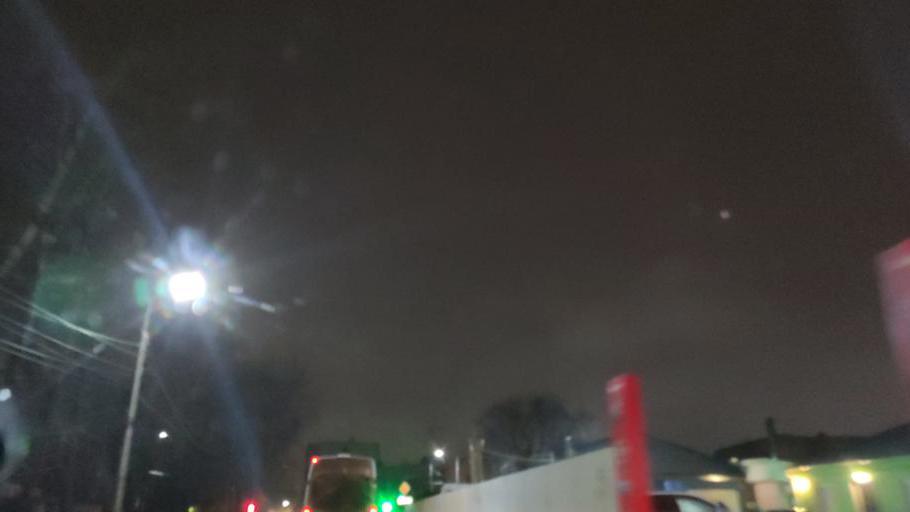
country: RU
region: Moskovskaya
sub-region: Podol'skiy Rayon
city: Podol'sk
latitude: 55.4340
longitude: 37.5714
